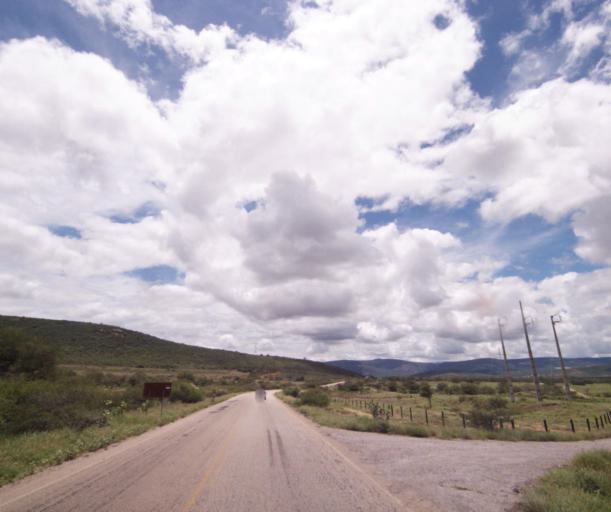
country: BR
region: Bahia
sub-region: Brumado
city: Brumado
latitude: -14.2000
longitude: -41.6030
